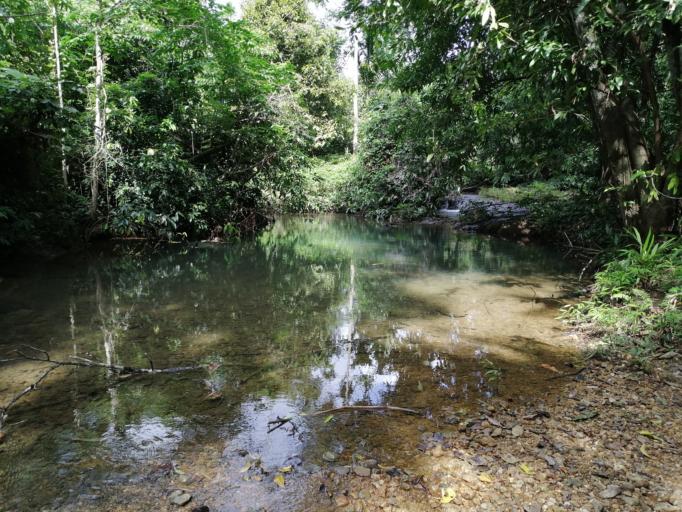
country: TH
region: Phatthalung
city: Pa Phayom
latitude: 7.9103
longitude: 99.7833
